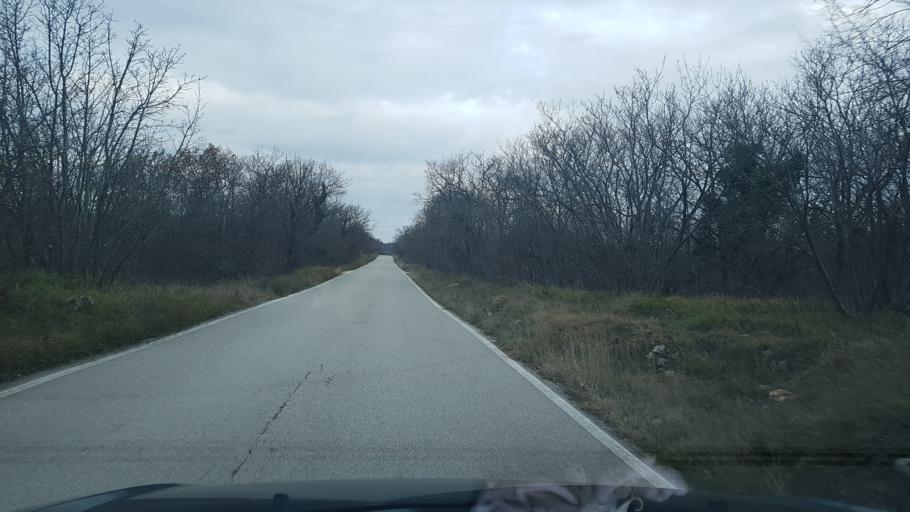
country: IT
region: Friuli Venezia Giulia
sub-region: Provincia di Trieste
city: Zolla
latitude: 45.7050
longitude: 13.8233
